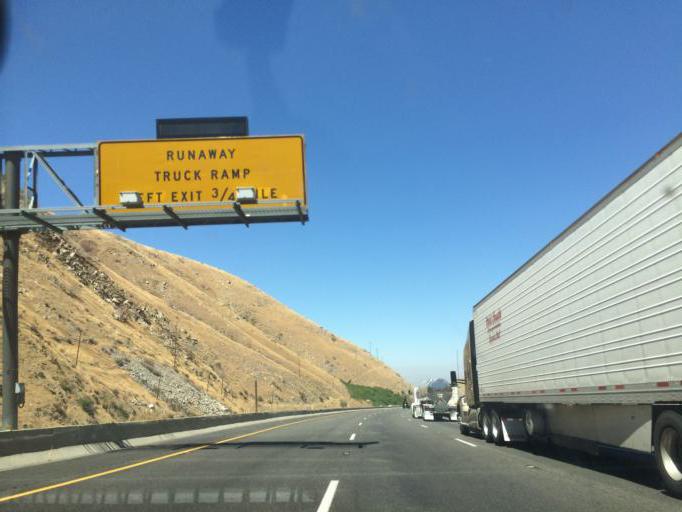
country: US
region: California
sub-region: Kern County
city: Frazier Park
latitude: 34.9064
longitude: -118.9236
